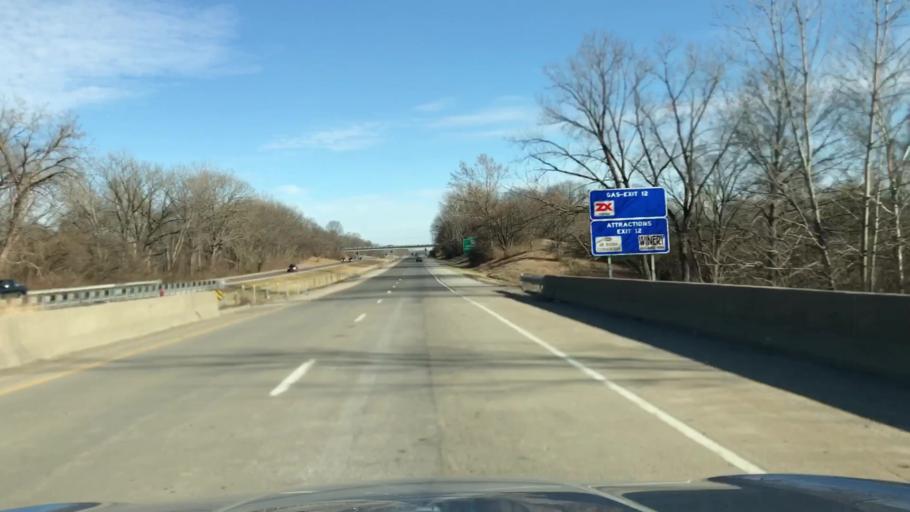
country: US
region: Illinois
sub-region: Madison County
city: Glen Carbon
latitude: 38.7567
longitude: -89.9807
